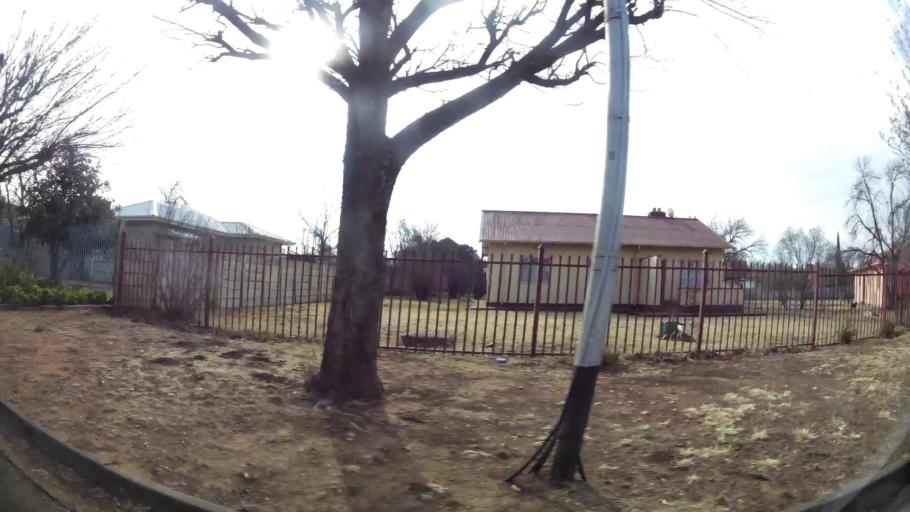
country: ZA
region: Orange Free State
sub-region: Mangaung Metropolitan Municipality
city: Bloemfontein
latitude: -29.0820
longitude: 26.2427
